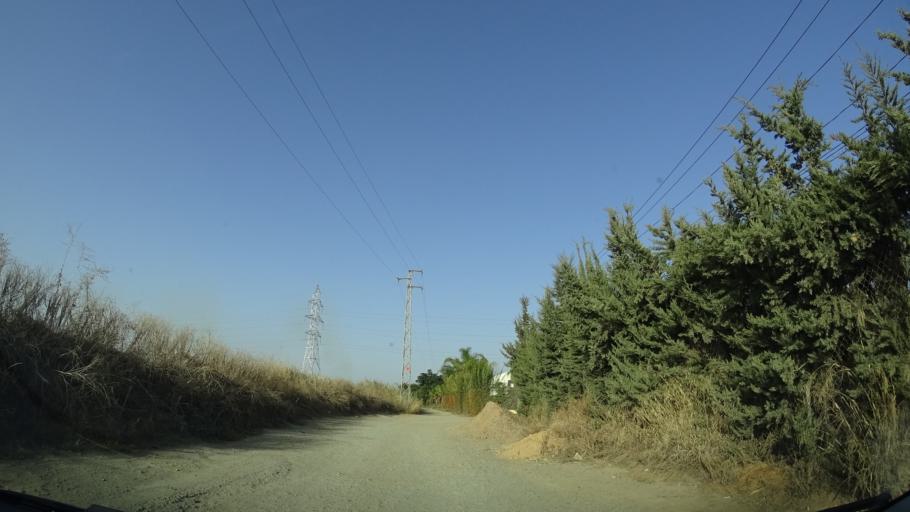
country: ES
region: Andalusia
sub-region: Provincia de Sevilla
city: La Algaba
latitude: 37.4404
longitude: -5.9829
